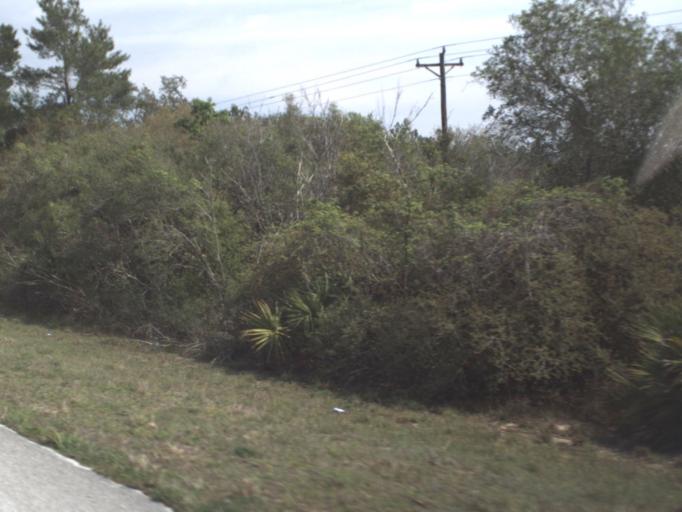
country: US
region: Florida
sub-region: Lake County
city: Astor
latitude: 29.2297
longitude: -81.6461
